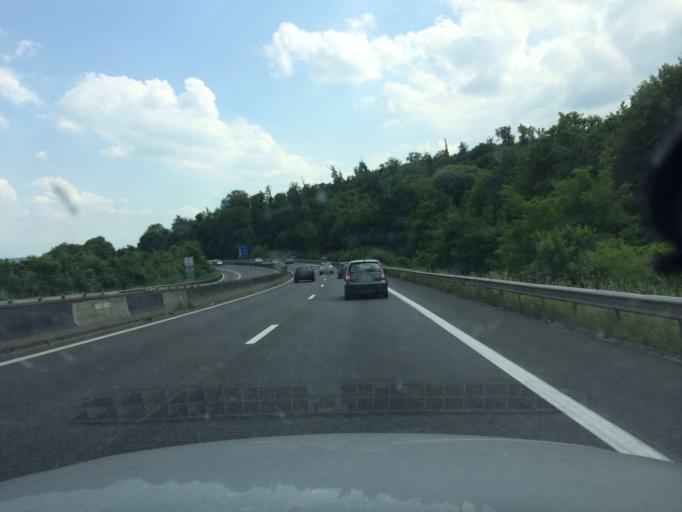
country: FR
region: Lorraine
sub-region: Departement de Meurthe-et-Moselle
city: Vandoeuvre-les-Nancy
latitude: 48.6383
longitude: 6.1710
